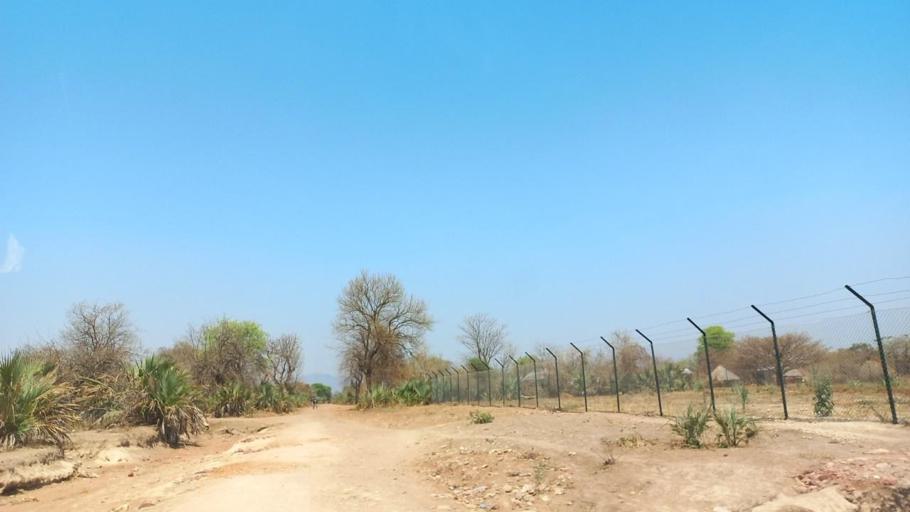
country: ZM
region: Lusaka
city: Luangwa
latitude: -15.1867
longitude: 30.2158
